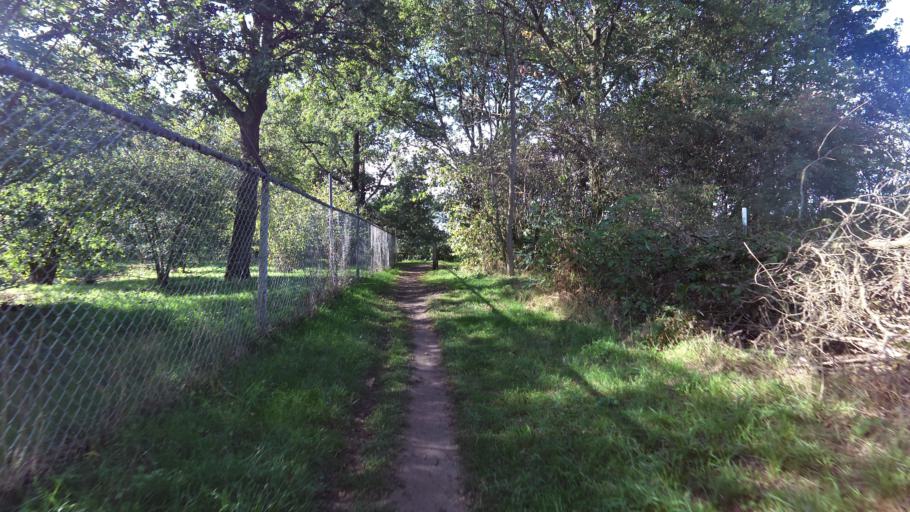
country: NL
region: Gelderland
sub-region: Gemeente Renkum
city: Heelsum
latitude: 51.9907
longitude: 5.7602
